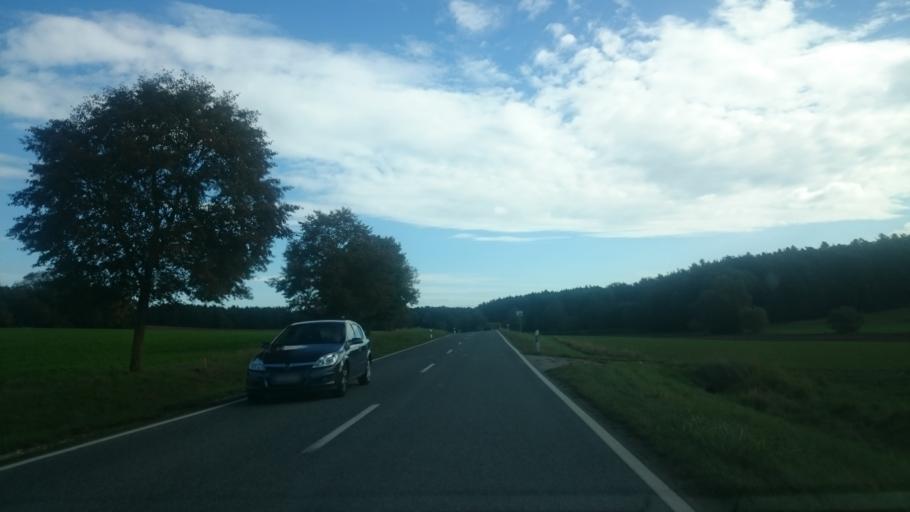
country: DE
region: Bavaria
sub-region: Regierungsbezirk Mittelfranken
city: Hilpoltstein
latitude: 49.1506
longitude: 11.2237
